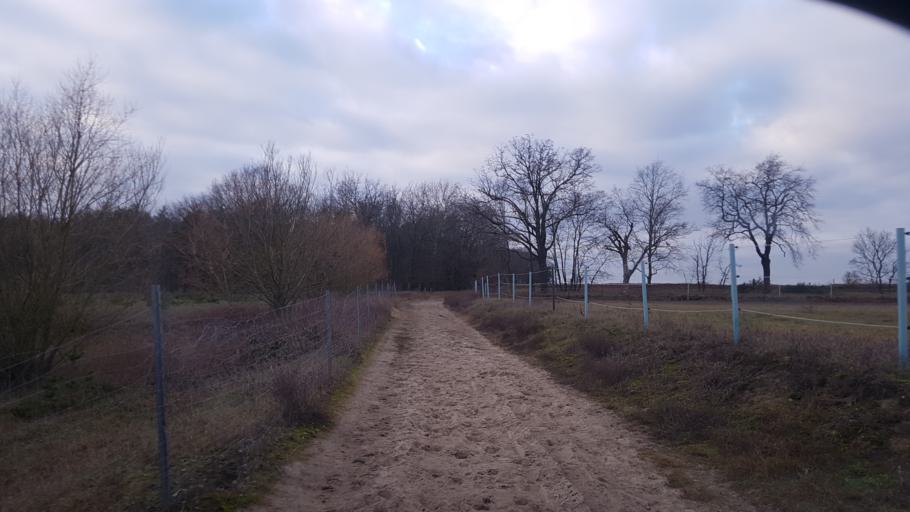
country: DE
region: Brandenburg
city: Ludwigsfelde
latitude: 52.3330
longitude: 13.2171
